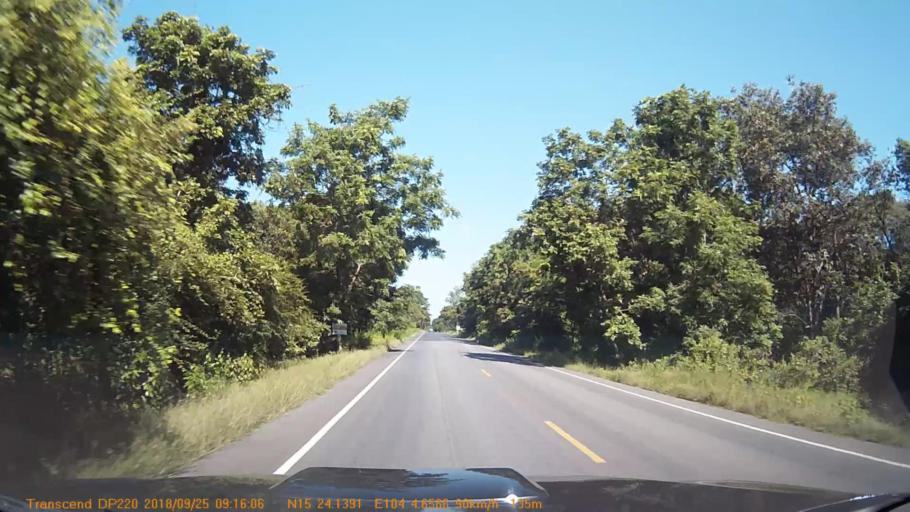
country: TH
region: Sisaket
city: Sila Lat
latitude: 15.4022
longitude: 104.0779
